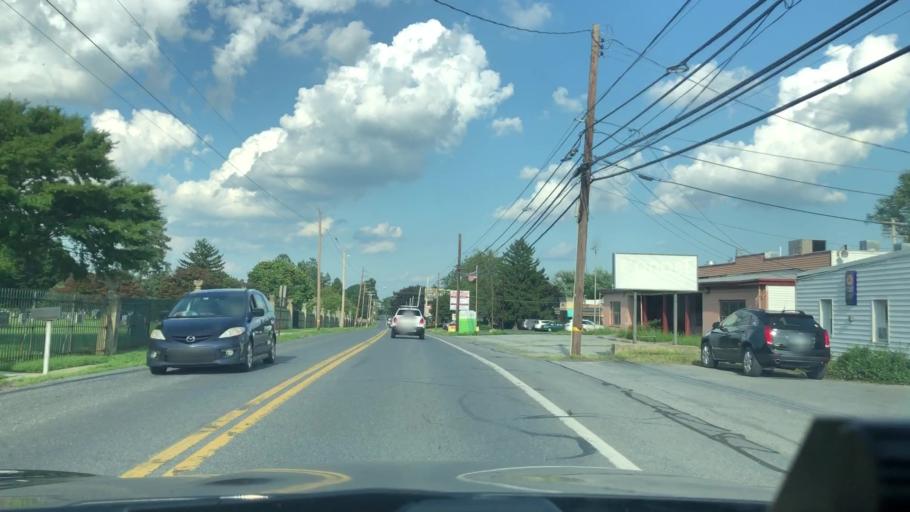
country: US
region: Pennsylvania
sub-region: Lehigh County
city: Allentown
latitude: 40.6161
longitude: -75.5271
